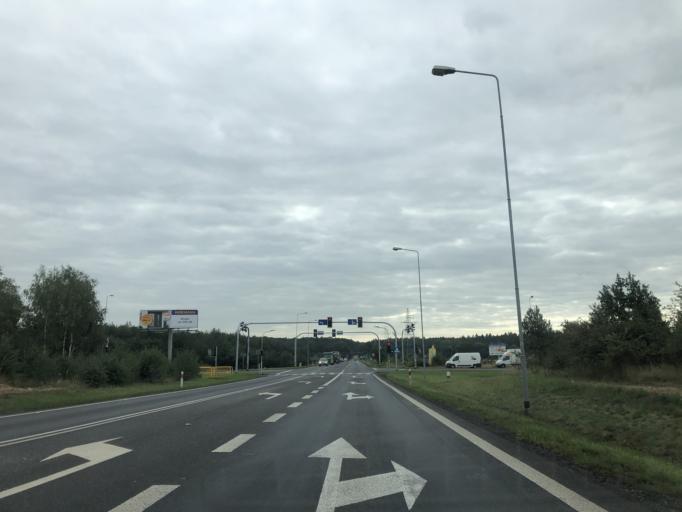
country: PL
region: Greater Poland Voivodeship
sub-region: Powiat pilski
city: Pila
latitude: 53.1872
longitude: 16.7604
